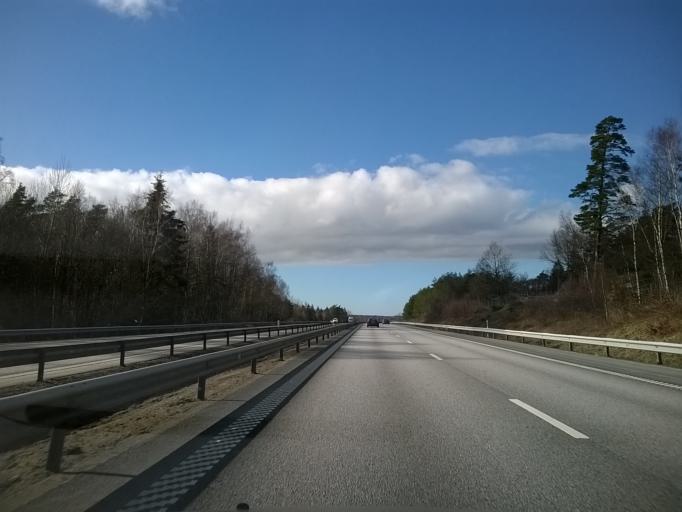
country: SE
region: Halland
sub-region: Kungsbacka Kommun
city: Kungsbacka
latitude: 57.4461
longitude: 12.1063
